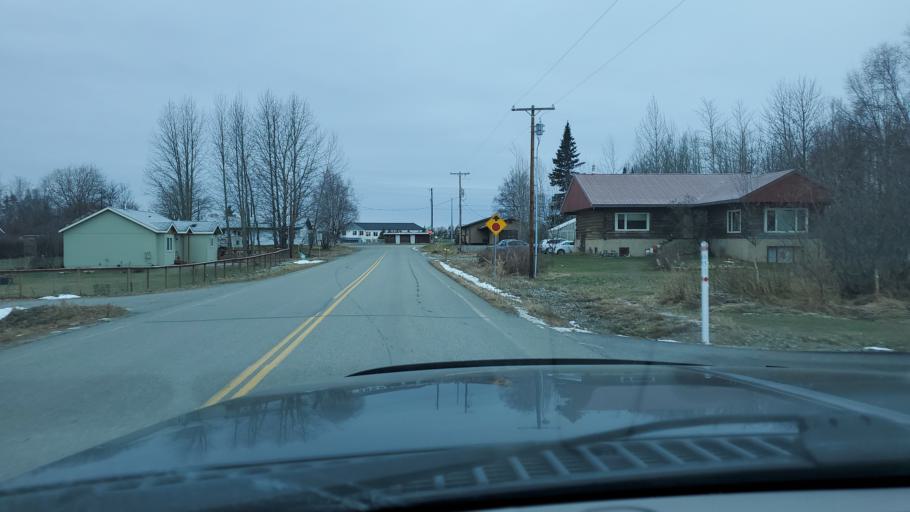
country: US
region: Alaska
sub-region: Matanuska-Susitna Borough
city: Palmer
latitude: 61.5995
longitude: -149.1004
